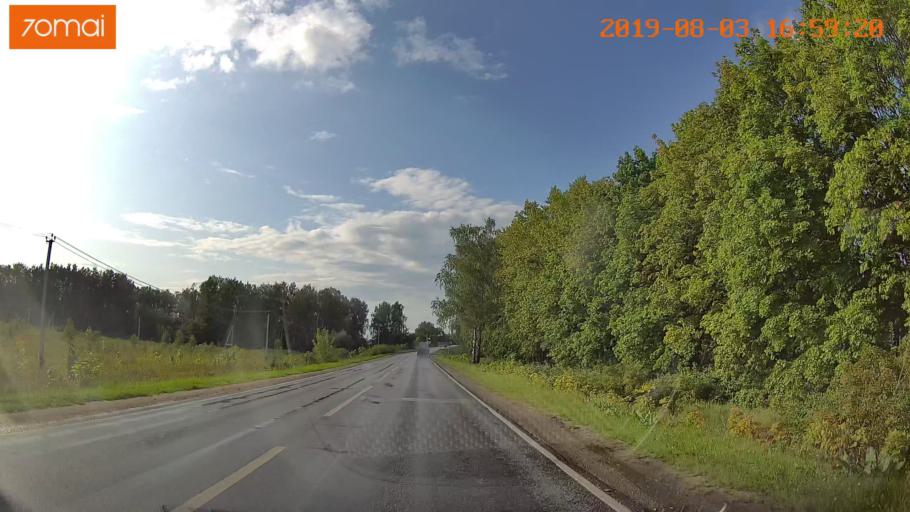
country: RU
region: Moskovskaya
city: Voskresensk
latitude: 55.3290
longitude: 38.6252
